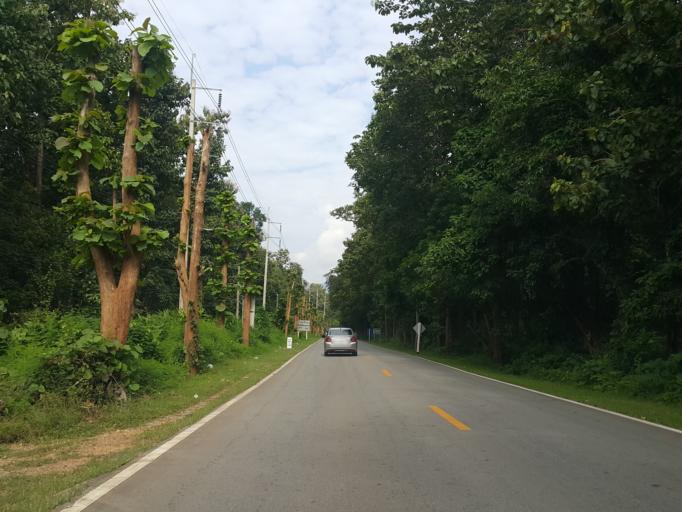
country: TH
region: Mae Hong Son
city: Mae Hong Son
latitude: 19.3692
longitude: 97.9638
